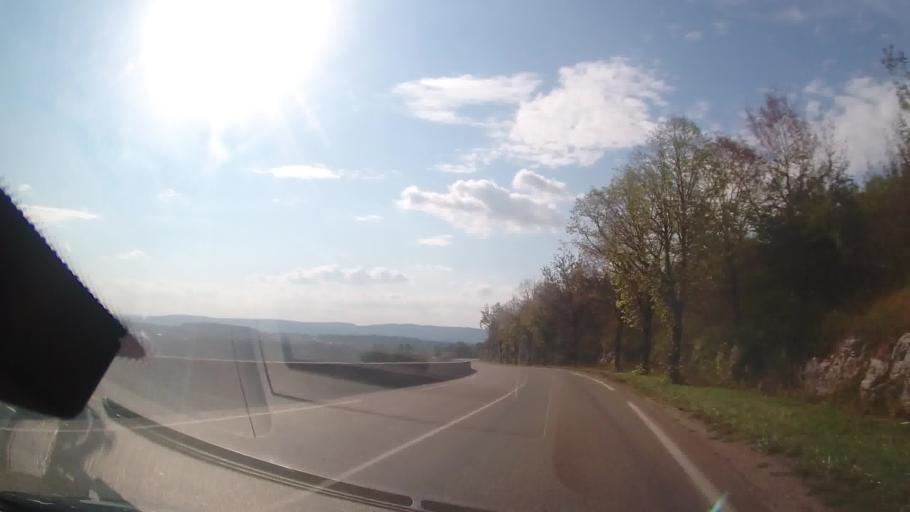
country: FR
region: Franche-Comte
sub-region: Departement du Jura
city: Clairvaux-les-Lacs
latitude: 46.5801
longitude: 5.7787
